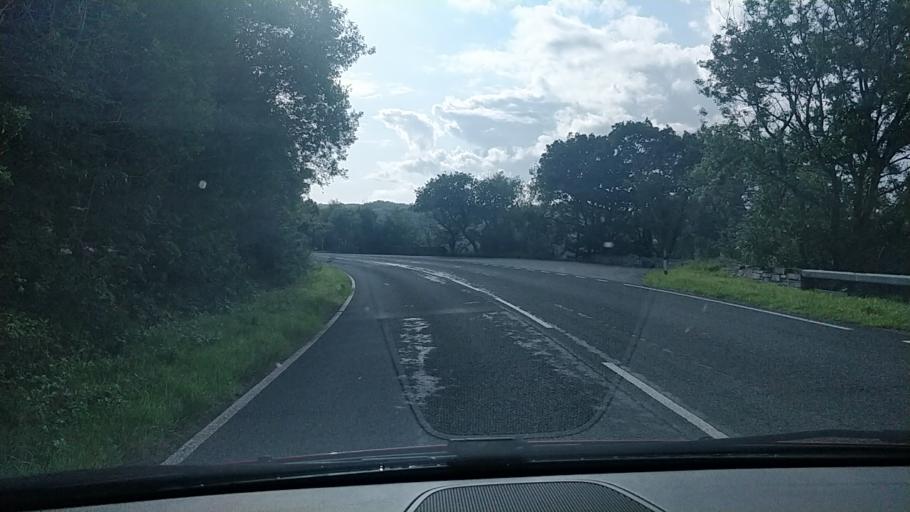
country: GB
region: Wales
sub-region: Gwynedd
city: Penrhyndeudraeth
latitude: 52.9362
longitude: -4.0294
